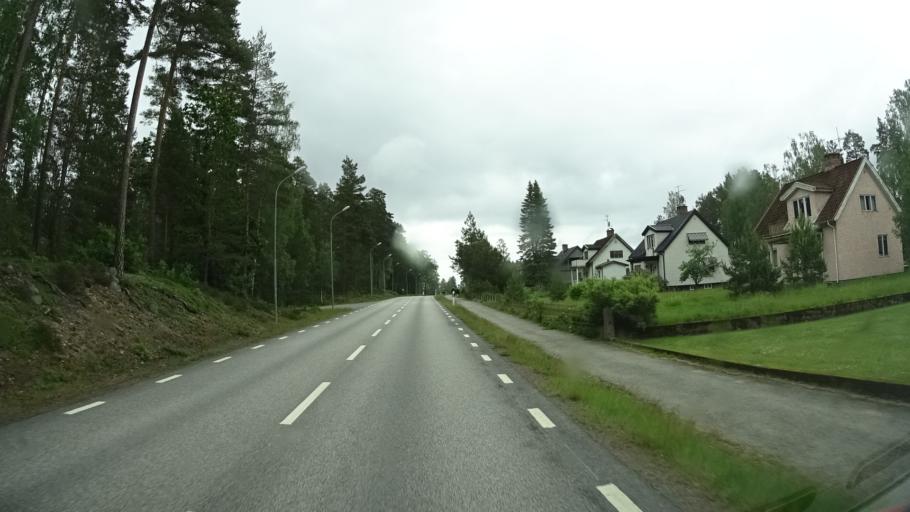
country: SE
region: Kalmar
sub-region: Hultsfreds Kommun
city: Hultsfred
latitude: 57.5450
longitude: 15.7409
